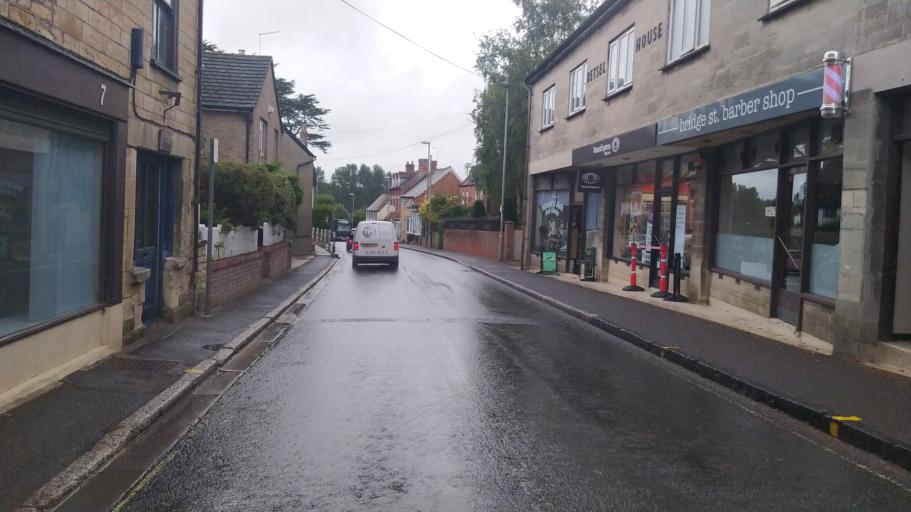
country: GB
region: England
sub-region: Dorset
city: Sturminster Newton
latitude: 50.9252
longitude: -2.3057
